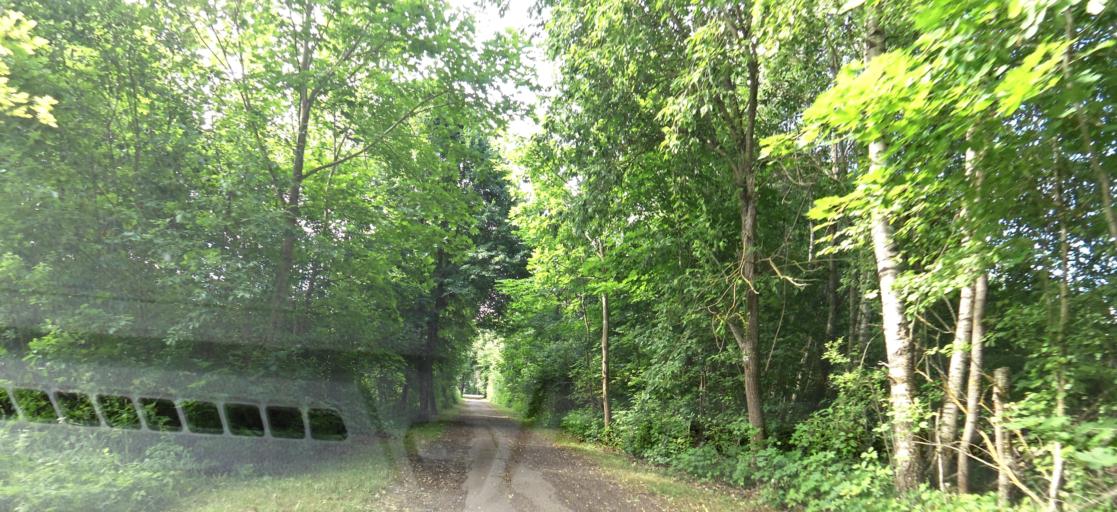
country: LT
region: Panevezys
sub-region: Birzai
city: Birzai
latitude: 56.2224
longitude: 24.7804
